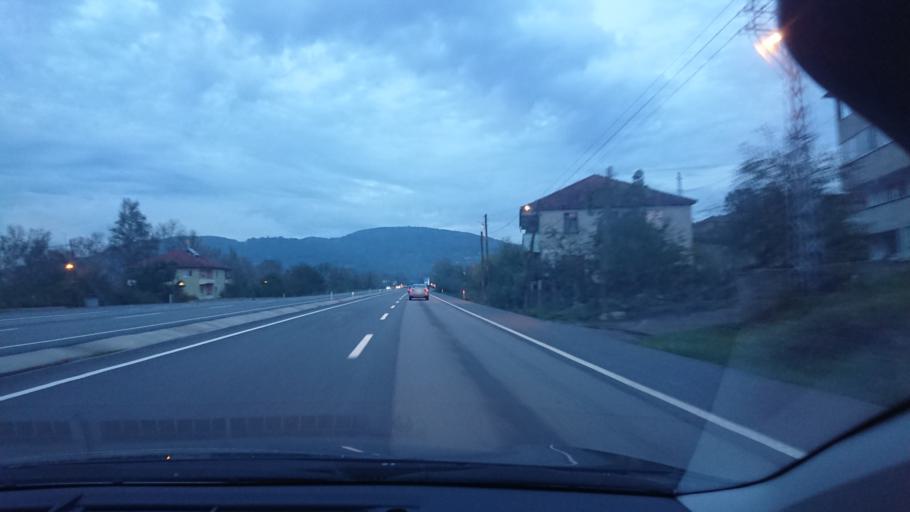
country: TR
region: Zonguldak
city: Gokcebey
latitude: 41.3344
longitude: 32.0745
